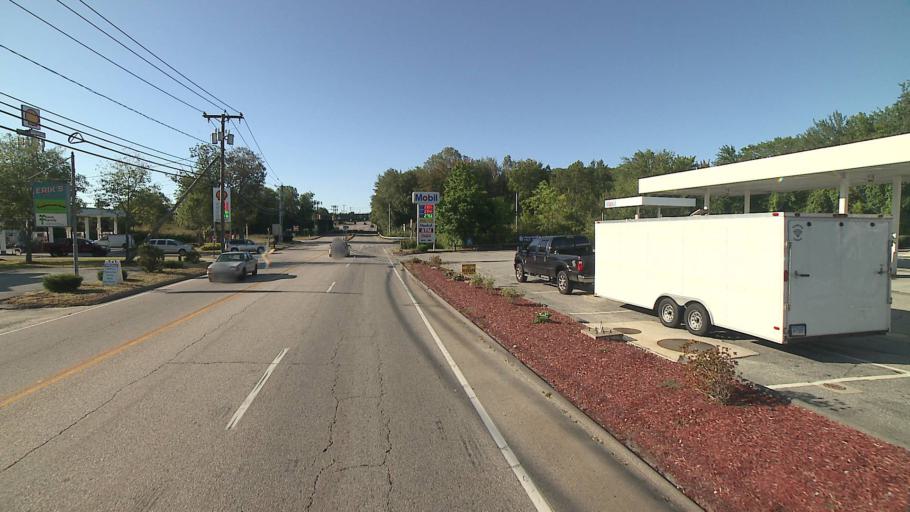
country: US
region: Connecticut
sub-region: New London County
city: Jewett City
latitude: 41.5908
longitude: -71.9910
